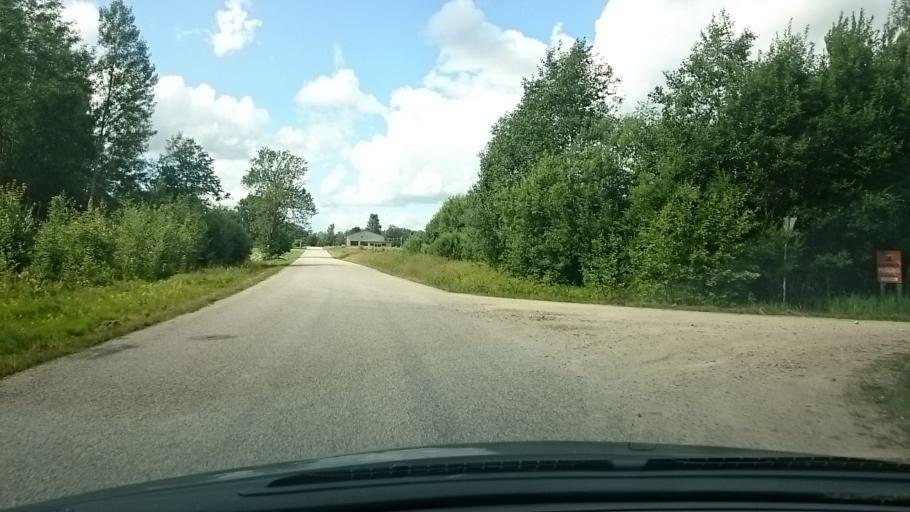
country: EE
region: Vorumaa
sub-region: Voru linn
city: Voru
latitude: 57.9228
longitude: 27.1308
